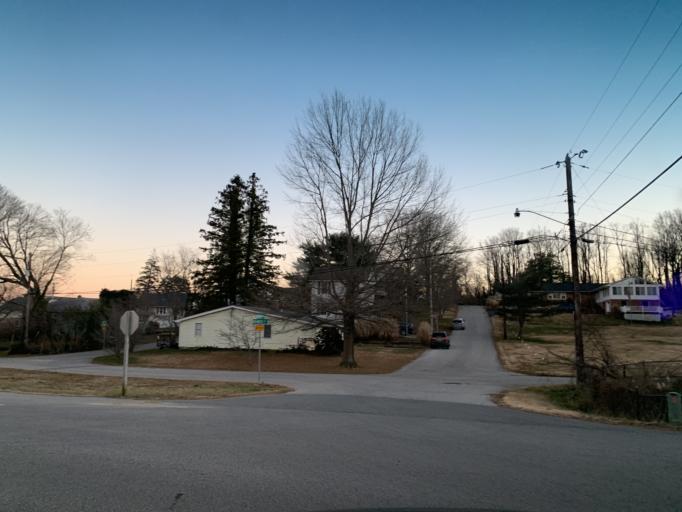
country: US
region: Maryland
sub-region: Calvert County
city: Prince Frederick
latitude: 38.5577
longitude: -76.5173
